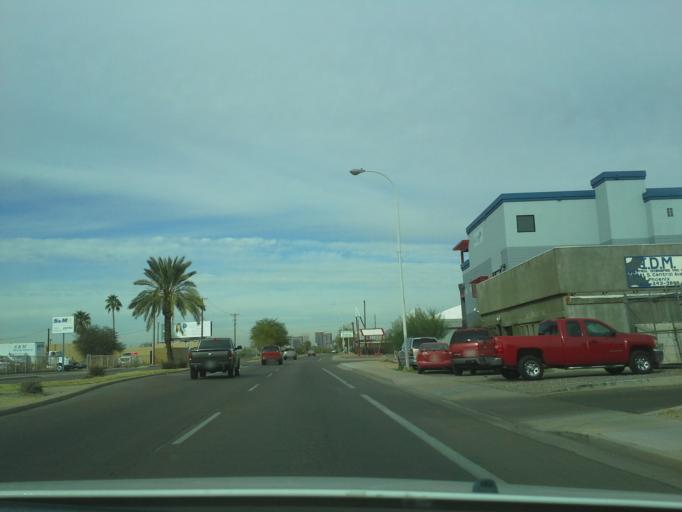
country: US
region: Arizona
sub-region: Maricopa County
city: Phoenix
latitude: 33.4155
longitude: -112.0734
